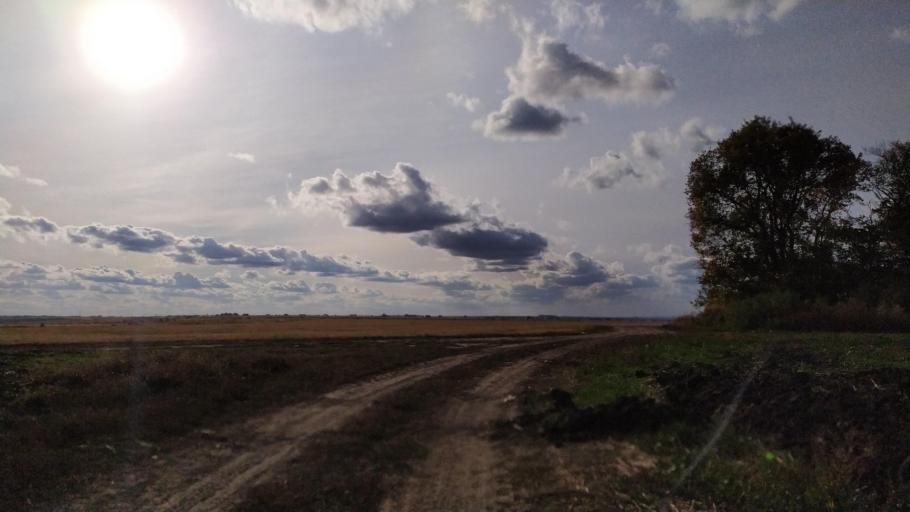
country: RU
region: Kursk
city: Kursk
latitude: 51.6118
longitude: 36.1666
